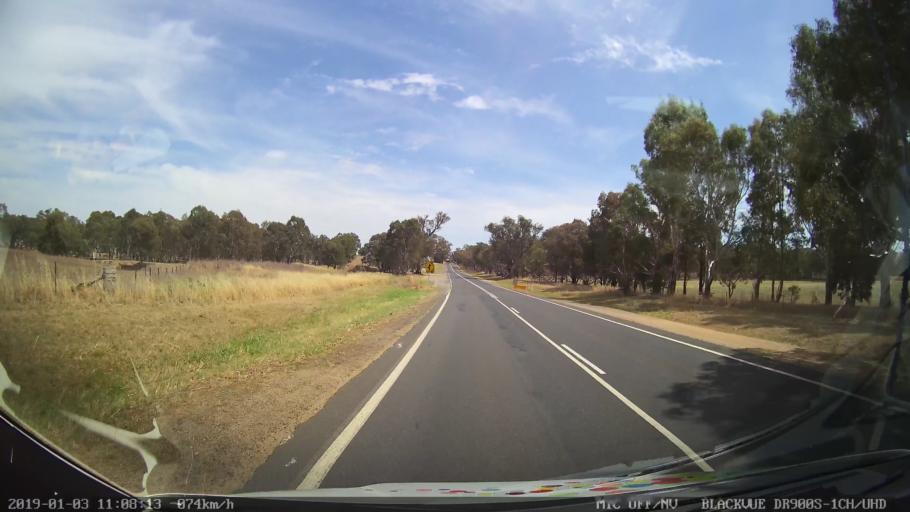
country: AU
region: New South Wales
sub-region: Young
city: Young
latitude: -34.2518
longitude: 148.2581
